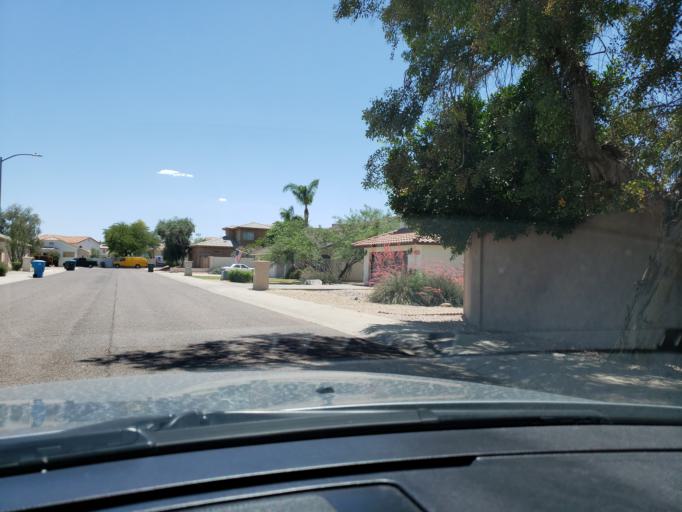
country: US
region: Arizona
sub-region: Maricopa County
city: Paradise Valley
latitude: 33.6158
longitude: -112.0166
